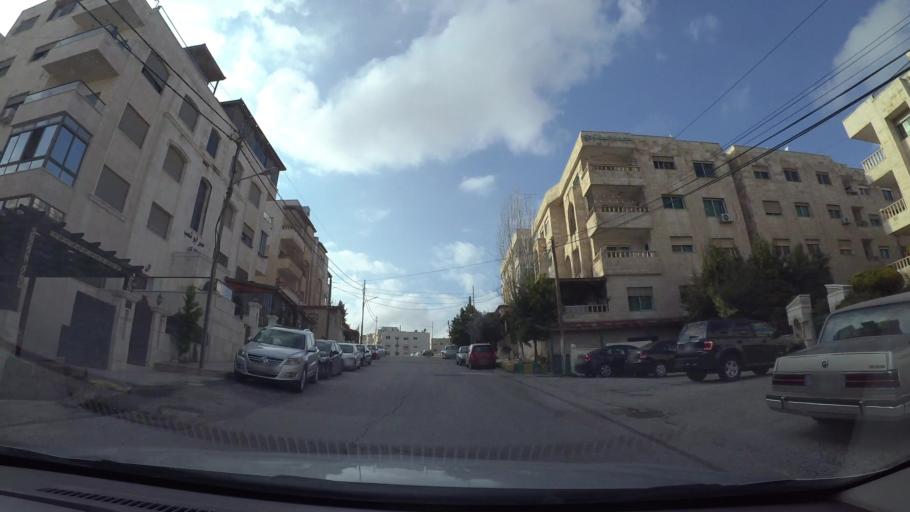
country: JO
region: Amman
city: Al Jubayhah
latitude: 31.9830
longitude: 35.8560
